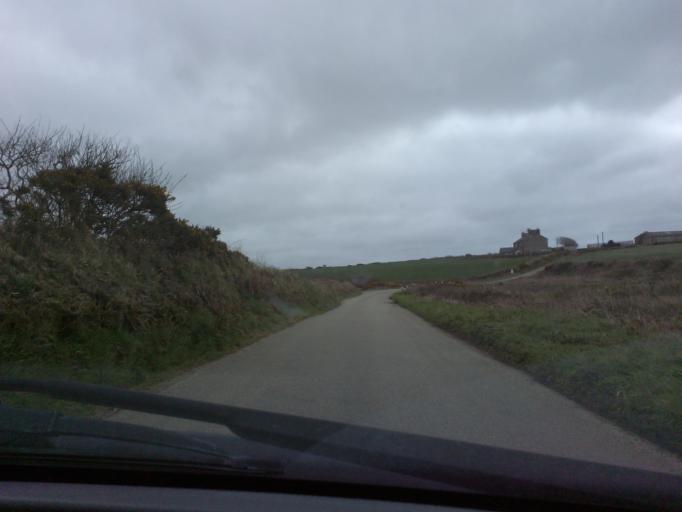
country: GB
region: England
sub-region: Cornwall
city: Penzance
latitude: 50.1519
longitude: -5.6080
